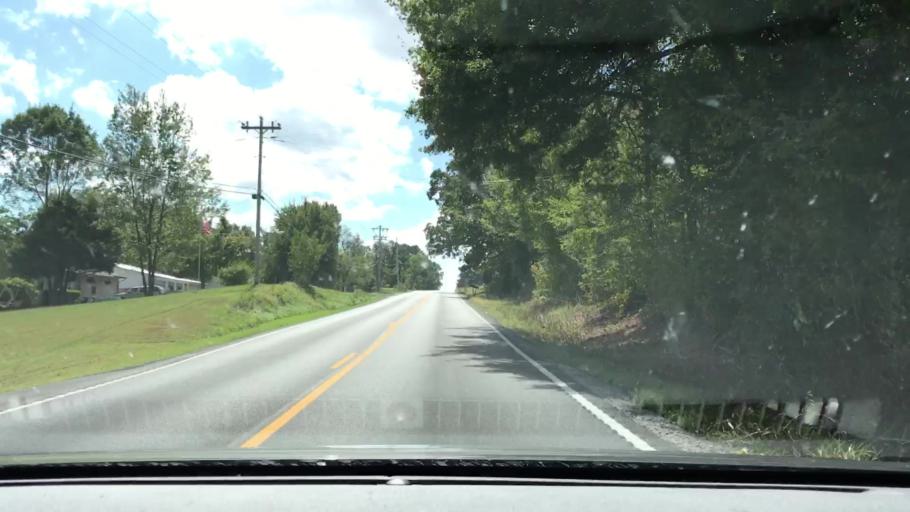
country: US
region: Kentucky
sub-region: Graves County
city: Mayfield
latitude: 36.7844
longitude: -88.5958
